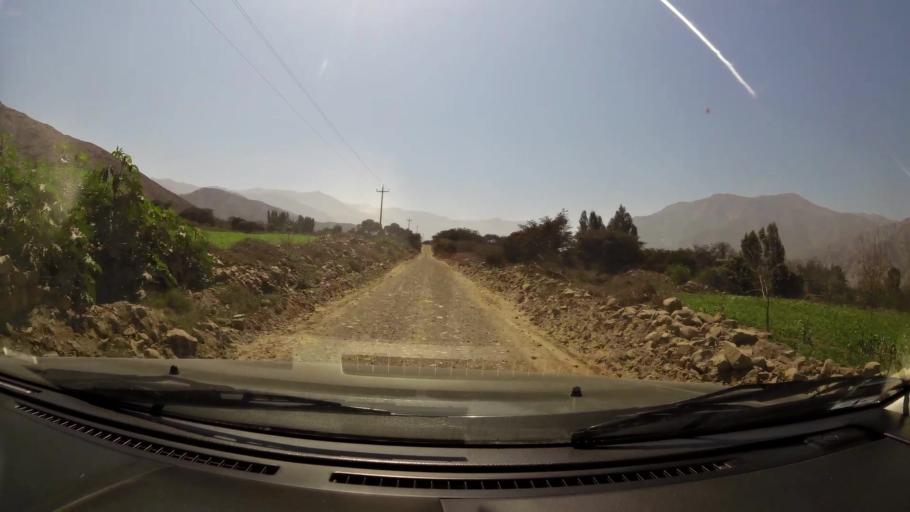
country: PE
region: Ica
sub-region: Provincia de Ica
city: Guadalupe
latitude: -13.8844
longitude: -75.6508
